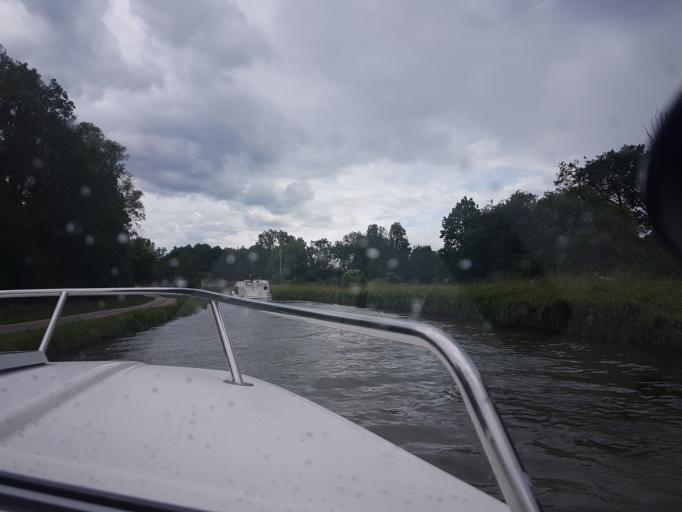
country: FR
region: Bourgogne
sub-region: Departement de la Nievre
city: Clamecy
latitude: 47.5515
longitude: 3.6310
